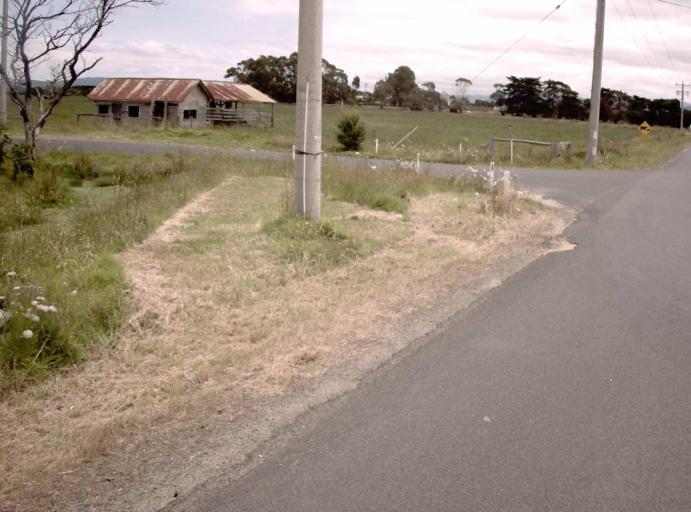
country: AU
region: Victoria
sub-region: Latrobe
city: Traralgon
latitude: -38.5531
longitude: 146.6544
